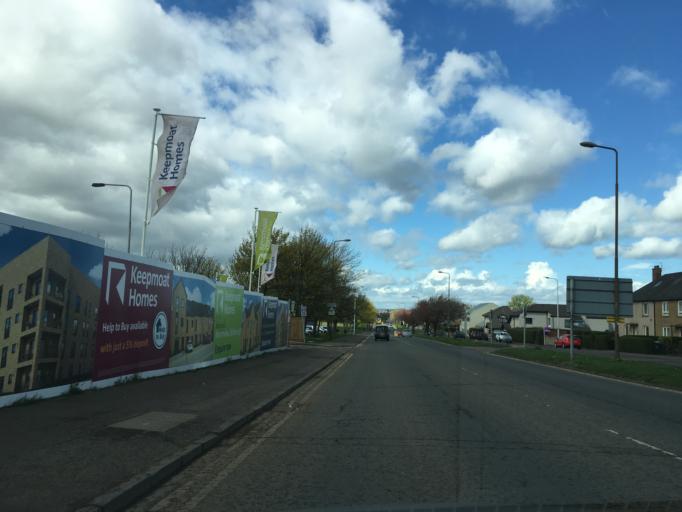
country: GB
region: Scotland
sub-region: Edinburgh
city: Colinton
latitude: 55.9249
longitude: -3.2822
